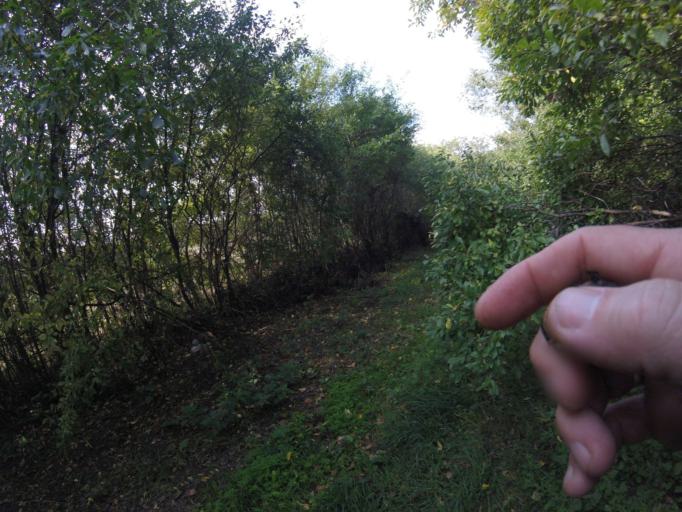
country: HU
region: Vas
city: Buk
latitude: 47.3239
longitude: 16.8217
